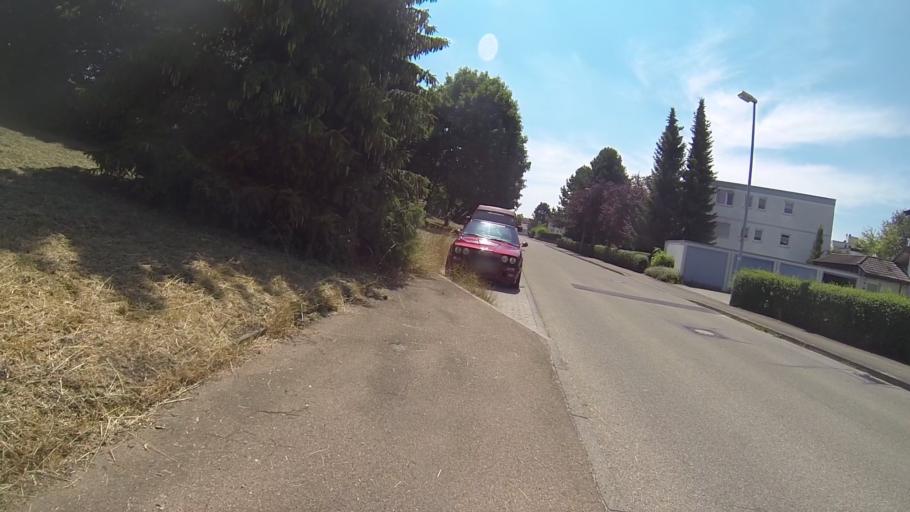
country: DE
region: Baden-Wuerttemberg
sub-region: Regierungsbezirk Stuttgart
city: Giengen an der Brenz
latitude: 48.6314
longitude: 10.2346
